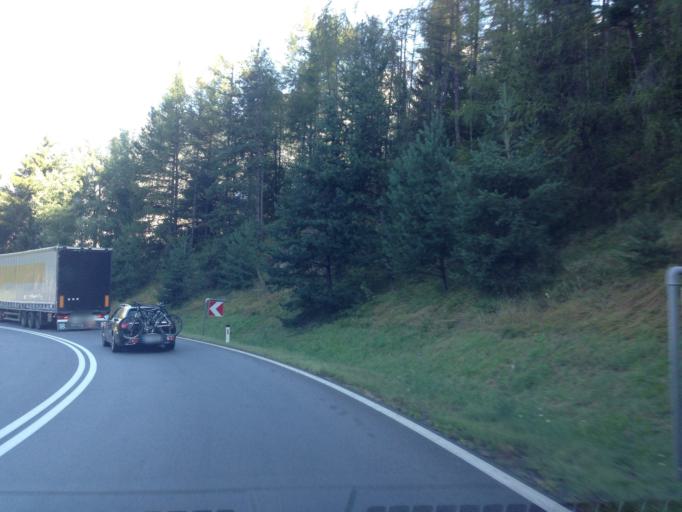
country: AT
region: Tyrol
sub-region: Politischer Bezirk Imst
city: Nassereith
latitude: 47.3056
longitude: 10.8575
